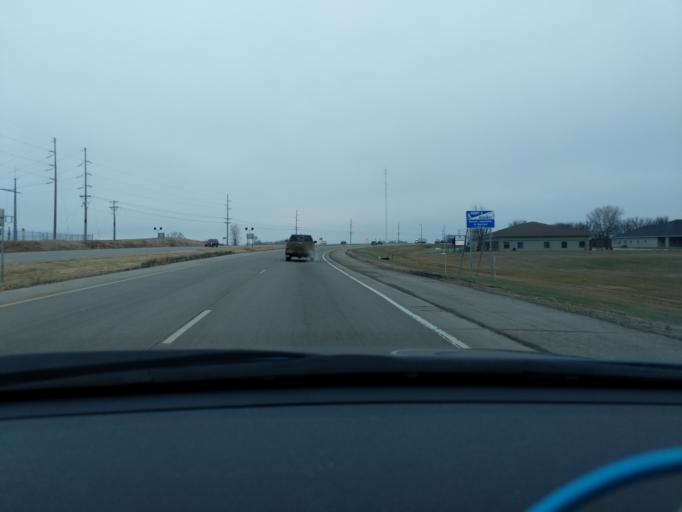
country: US
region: Minnesota
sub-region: Lyon County
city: Marshall
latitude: 44.4495
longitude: -95.7563
